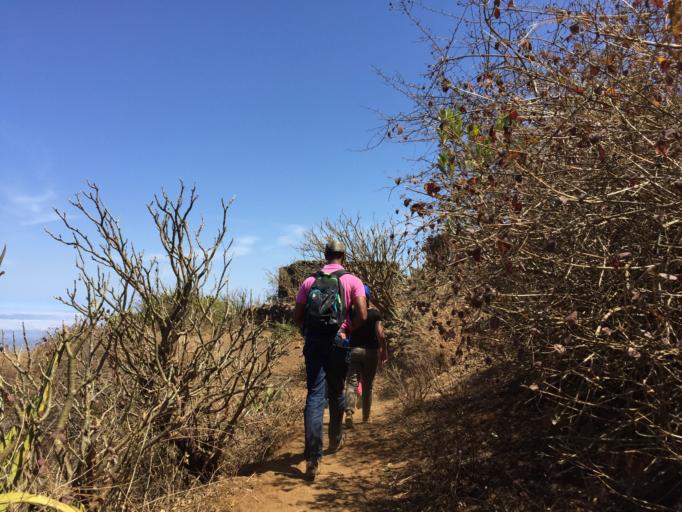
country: CV
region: Mosteiros
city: Porto dos Mosteiros
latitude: 15.0086
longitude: -24.3894
